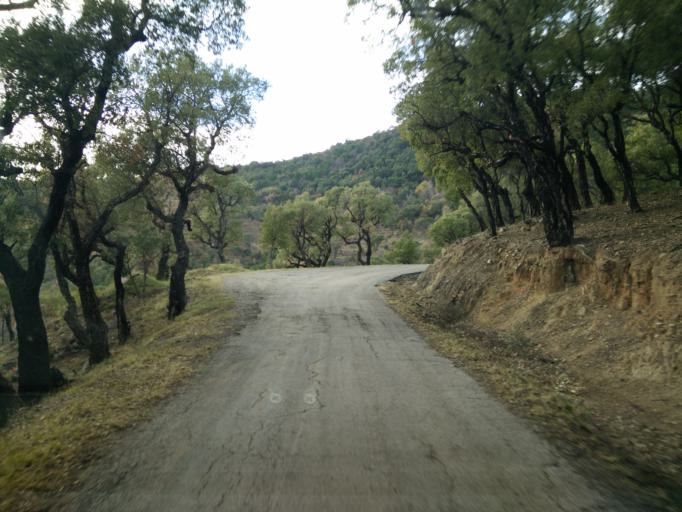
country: FR
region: Provence-Alpes-Cote d'Azur
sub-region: Departement du Var
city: Roquebrune-sur-Argens
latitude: 43.4072
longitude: 6.6328
